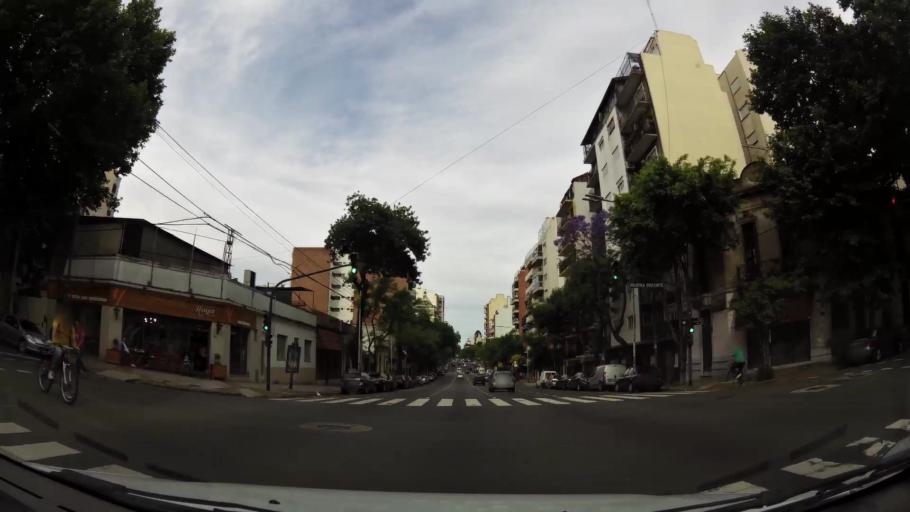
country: AR
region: Buenos Aires F.D.
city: Villa Santa Rita
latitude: -34.6335
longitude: -58.4608
